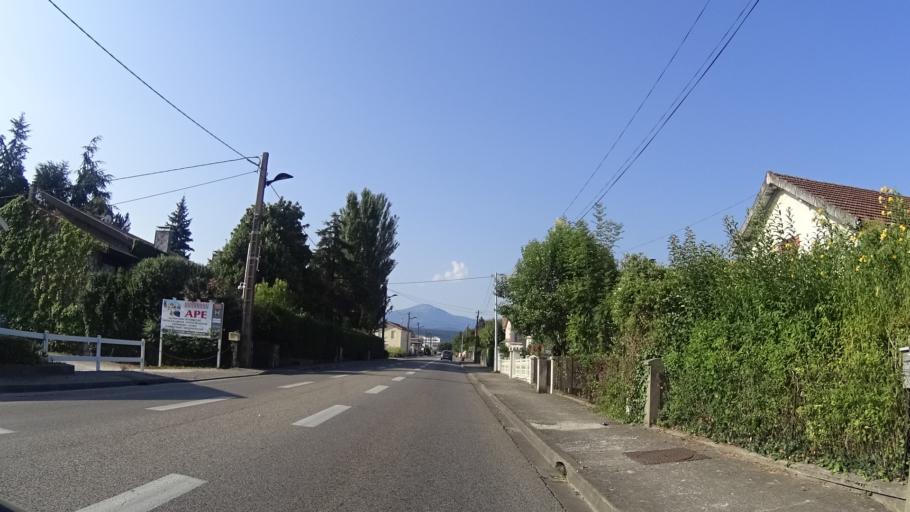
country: FR
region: Midi-Pyrenees
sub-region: Departement de l'Ariege
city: Lavelanet
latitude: 42.9669
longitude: 1.8654
